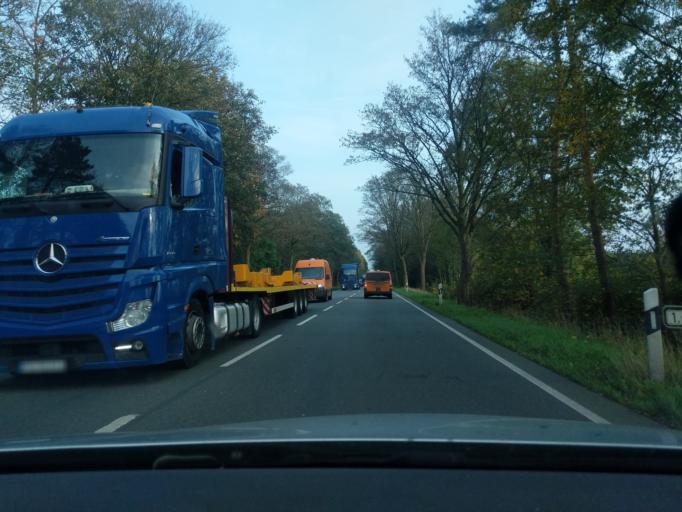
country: DE
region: Lower Saxony
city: Stade
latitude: 53.5832
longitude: 9.4781
